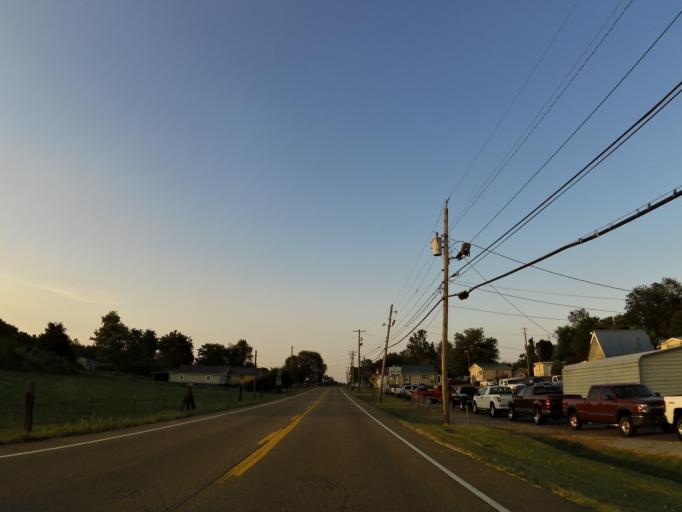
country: US
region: Tennessee
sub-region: Monroe County
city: Sweetwater
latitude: 35.6699
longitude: -84.4081
